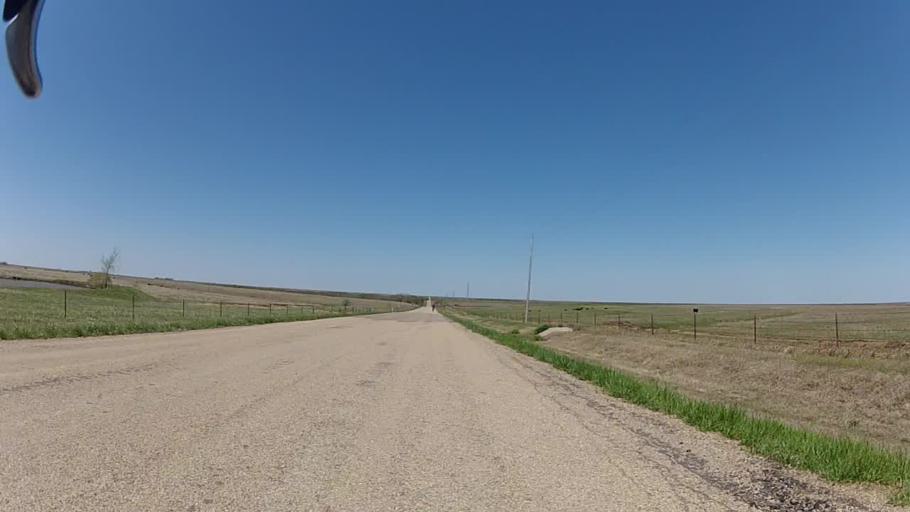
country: US
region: Kansas
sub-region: Riley County
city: Manhattan
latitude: 38.9716
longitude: -96.5350
